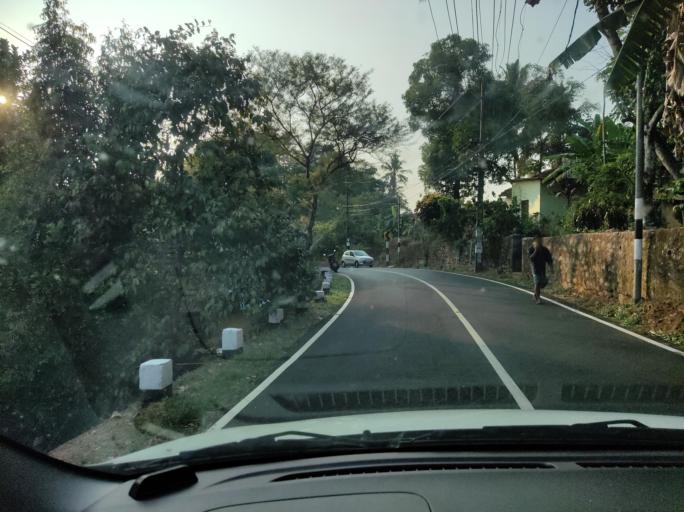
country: IN
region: Kerala
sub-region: Pattanamtitta
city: Tiruvalla
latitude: 9.3690
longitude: 76.5768
